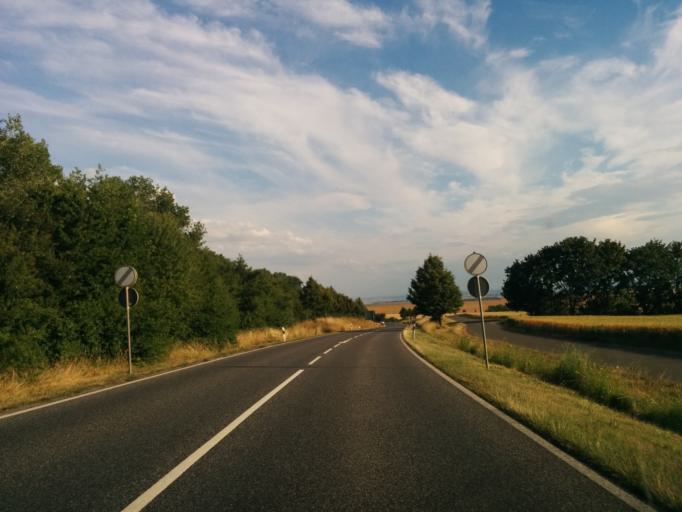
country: DE
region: Thuringia
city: Wasserthaleben
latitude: 51.2885
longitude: 10.8991
